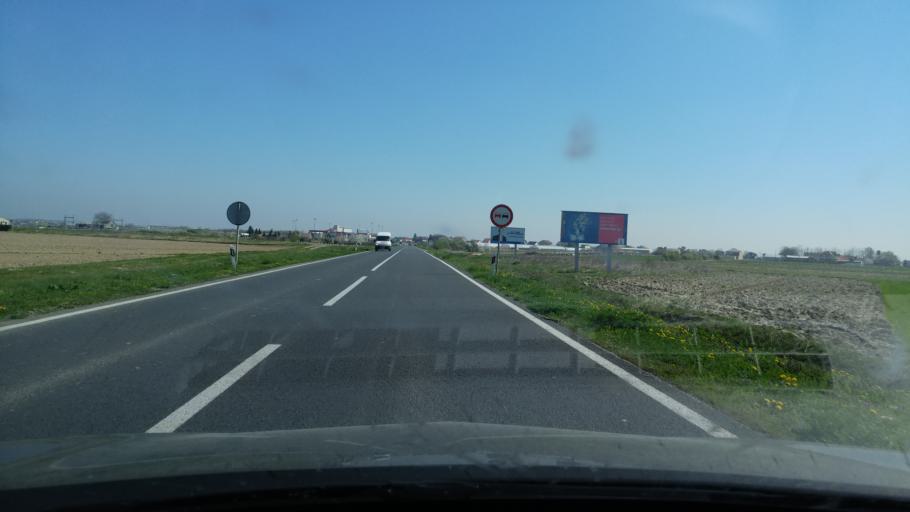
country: HR
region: Osjecko-Baranjska
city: Viskovci
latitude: 45.3315
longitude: 18.4096
